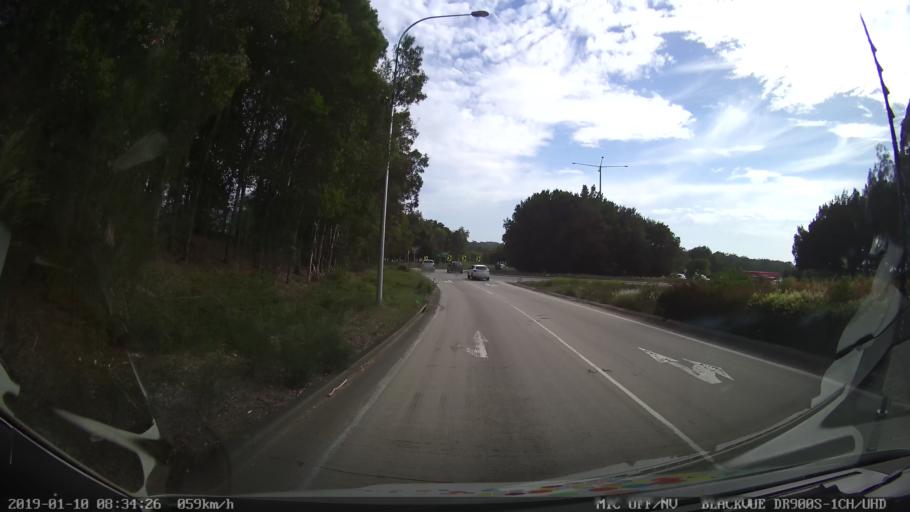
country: AU
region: New South Wales
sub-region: Coffs Harbour
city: Boambee
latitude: -30.3212
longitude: 153.0851
